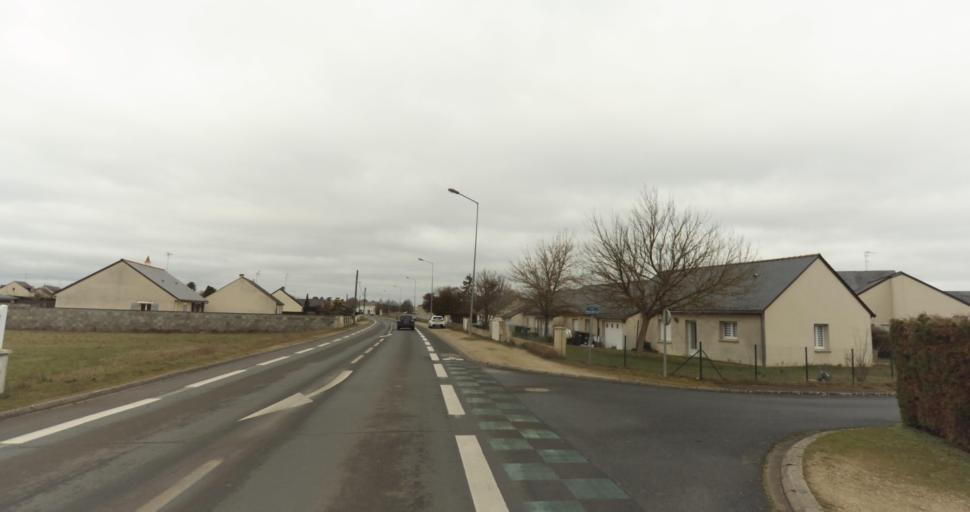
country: FR
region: Pays de la Loire
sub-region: Departement de Maine-et-Loire
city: Doue-la-Fontaine
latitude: 47.1864
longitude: -0.2687
